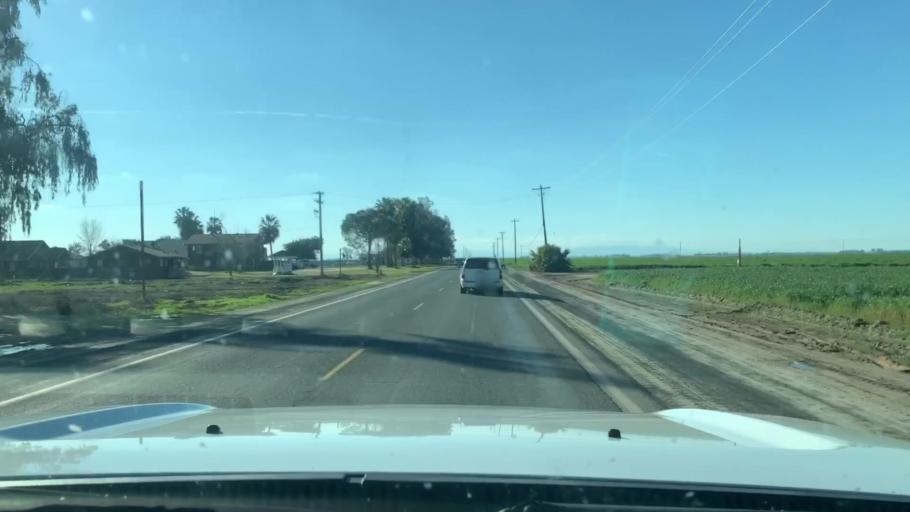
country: US
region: California
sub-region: Kings County
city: Armona
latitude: 36.2111
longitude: -119.7031
